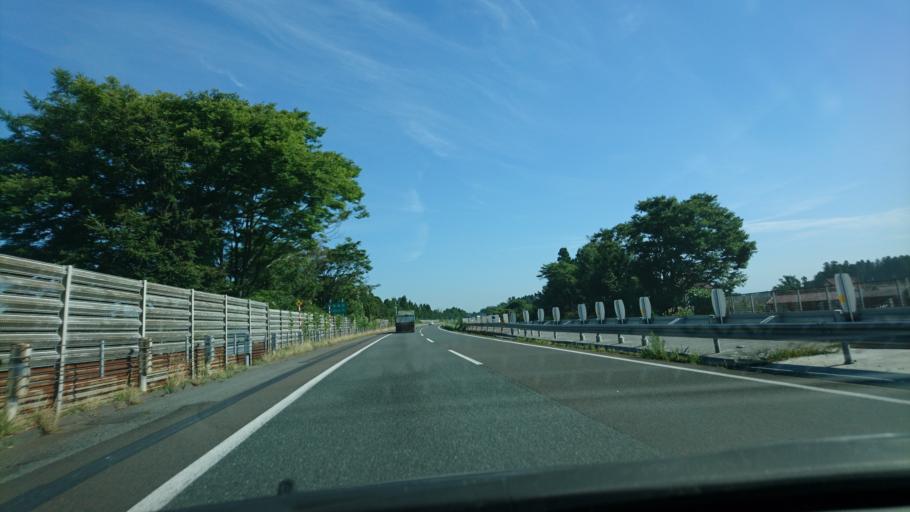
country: JP
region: Iwate
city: Mizusawa
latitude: 39.0763
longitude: 141.1000
